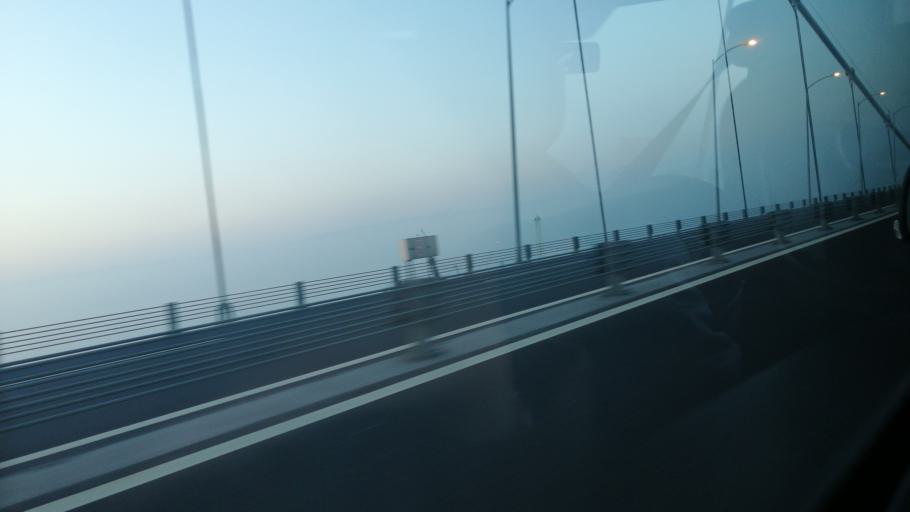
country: TR
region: Kocaeli
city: Tavsanli
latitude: 40.7647
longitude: 29.5174
